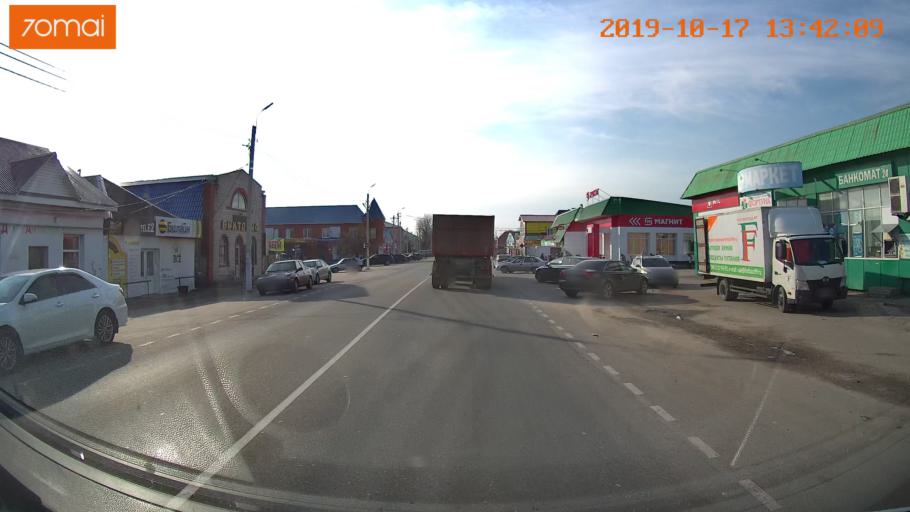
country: RU
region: Rjazan
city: Tuma
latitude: 55.1477
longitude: 40.5561
